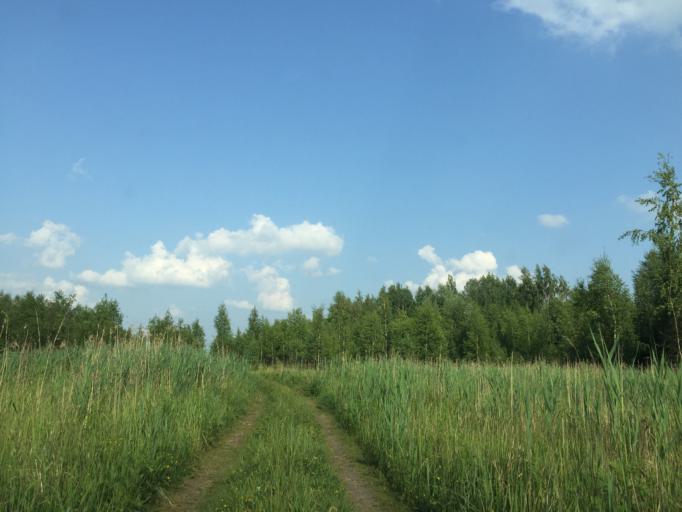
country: LV
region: Jelgava
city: Jelgava
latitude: 56.6726
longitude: 23.6583
